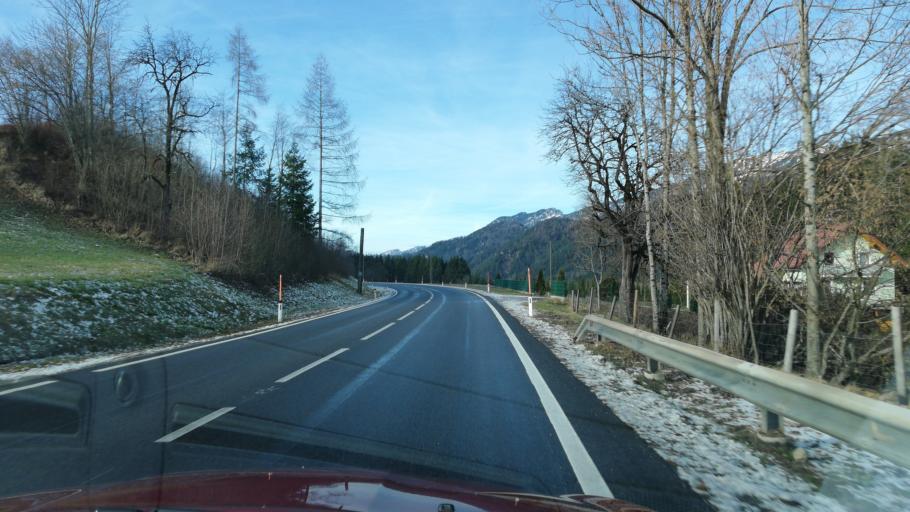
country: AT
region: Upper Austria
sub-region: Politischer Bezirk Kirchdorf an der Krems
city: Rossleithen
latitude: 47.7374
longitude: 14.2724
